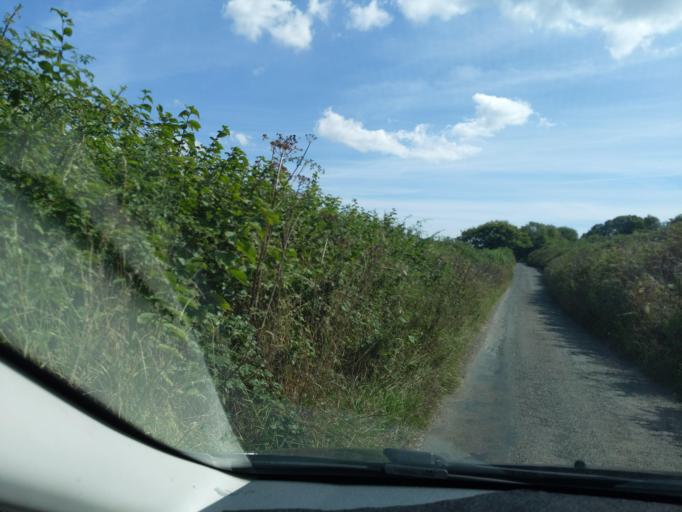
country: GB
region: England
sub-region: Cornwall
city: Torpoint
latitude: 50.3545
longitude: -4.2207
